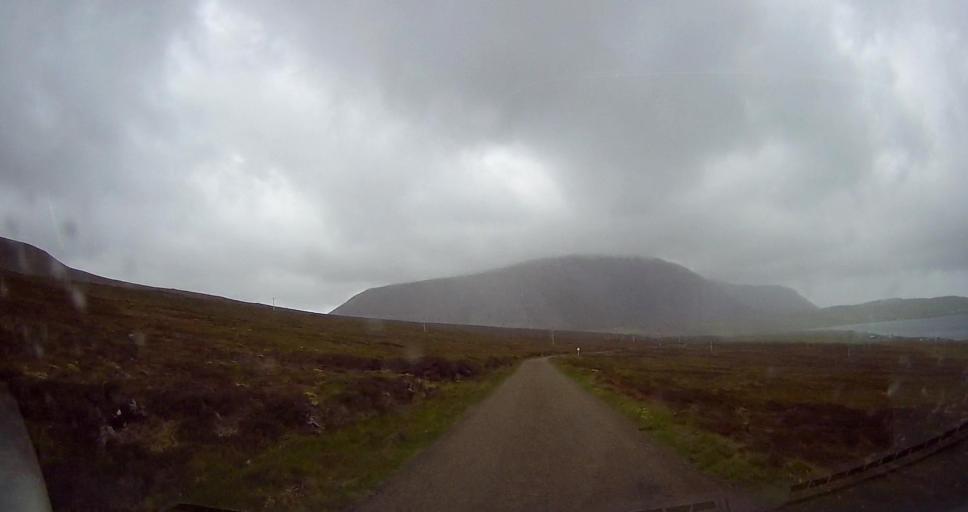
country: GB
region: Scotland
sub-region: Orkney Islands
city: Stromness
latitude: 58.9001
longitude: -3.2783
